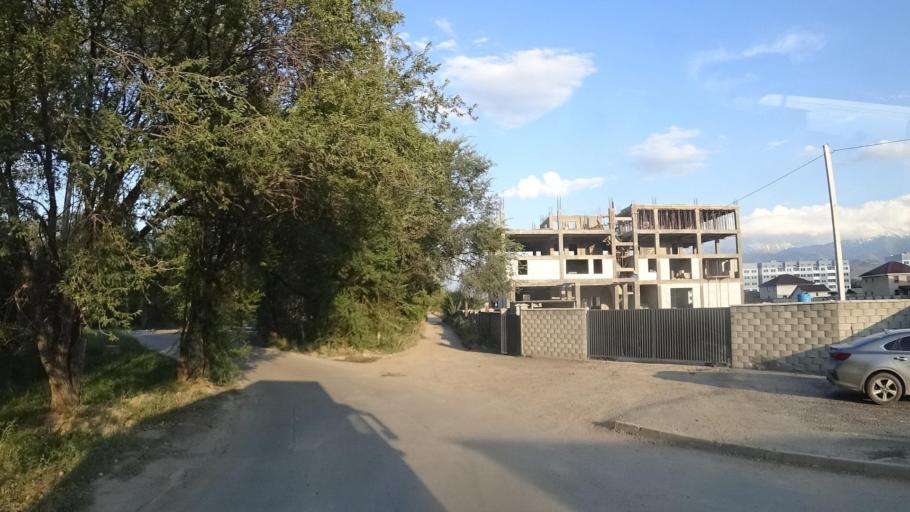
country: KZ
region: Almaty Oblysy
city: Pervomayskiy
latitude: 43.3283
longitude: 76.9848
